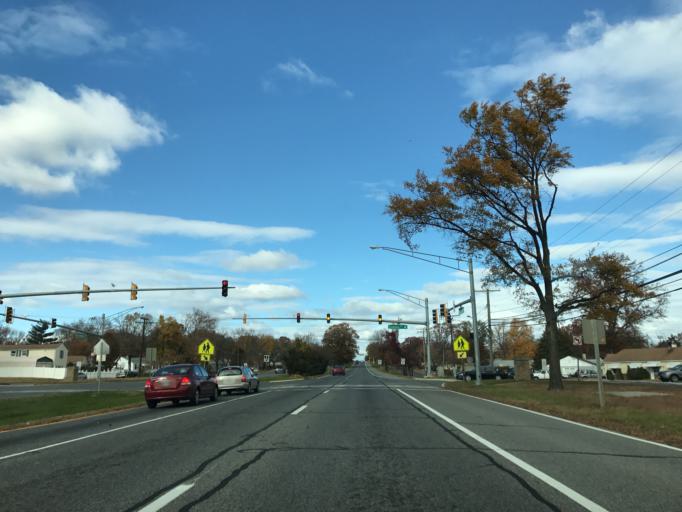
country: US
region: Maryland
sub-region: Anne Arundel County
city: Glen Burnie
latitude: 39.1533
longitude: -76.6141
